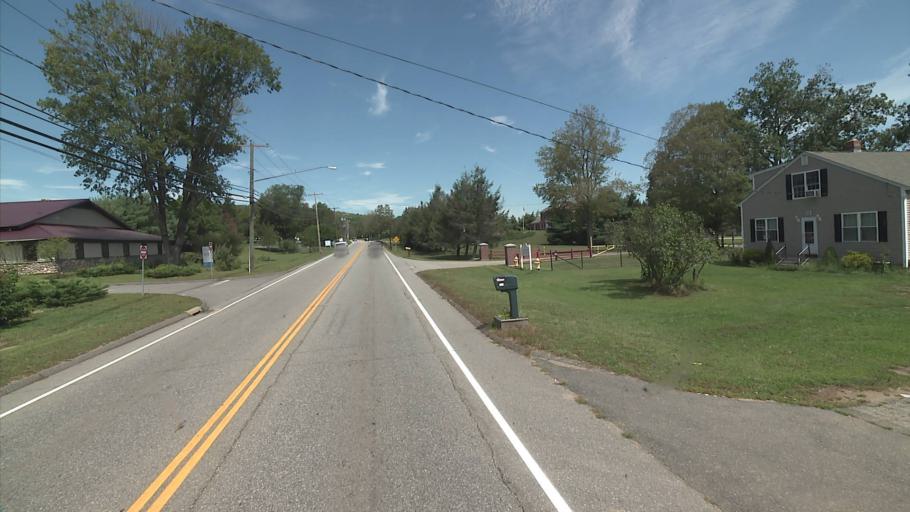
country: US
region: Connecticut
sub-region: Windham County
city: Willimantic
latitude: 41.7398
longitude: -72.1976
